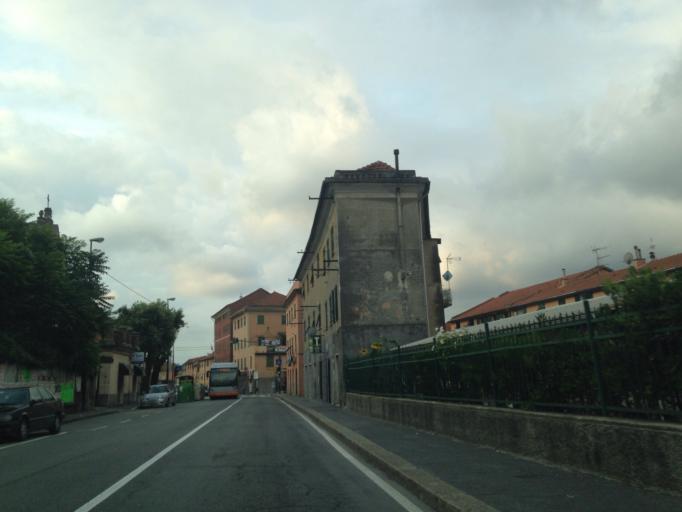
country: IT
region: Liguria
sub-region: Provincia di Genova
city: Santa Marta
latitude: 44.4867
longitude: 8.9003
